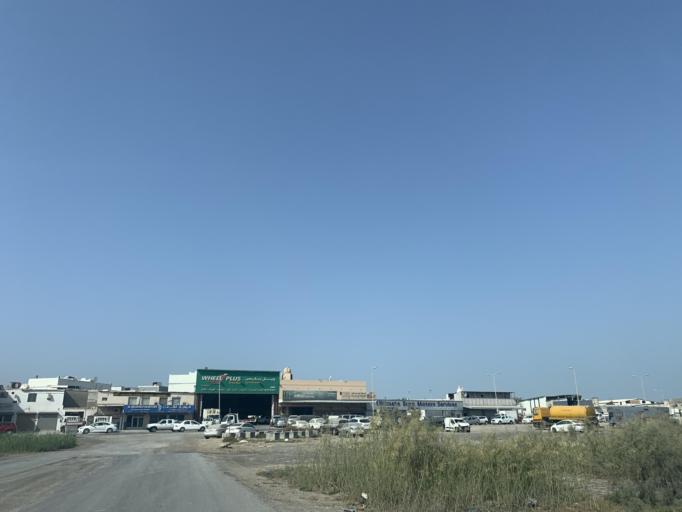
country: BH
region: Central Governorate
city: Madinat Hamad
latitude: 26.1370
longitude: 50.4864
